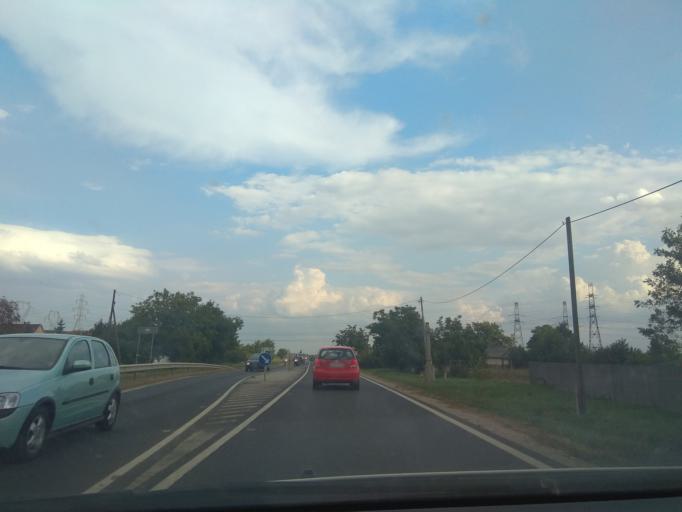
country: HU
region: Borsod-Abauj-Zemplen
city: Sajoszoged
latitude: 47.9418
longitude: 20.9991
